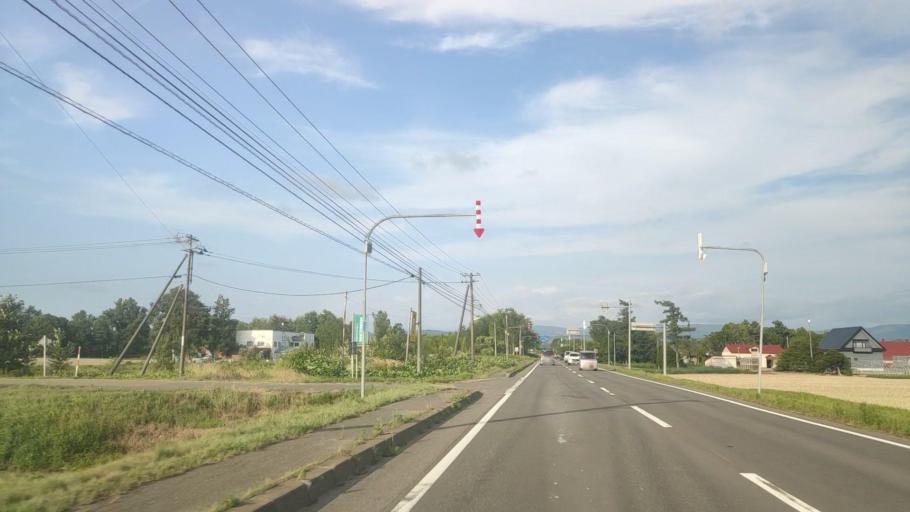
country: JP
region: Hokkaido
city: Iwamizawa
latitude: 43.0217
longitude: 141.8039
